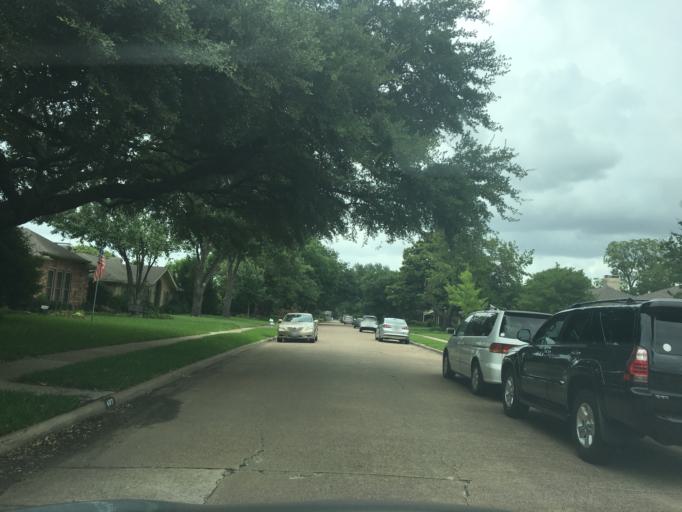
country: US
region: Texas
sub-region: Dallas County
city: Richardson
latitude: 32.9314
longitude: -96.7326
